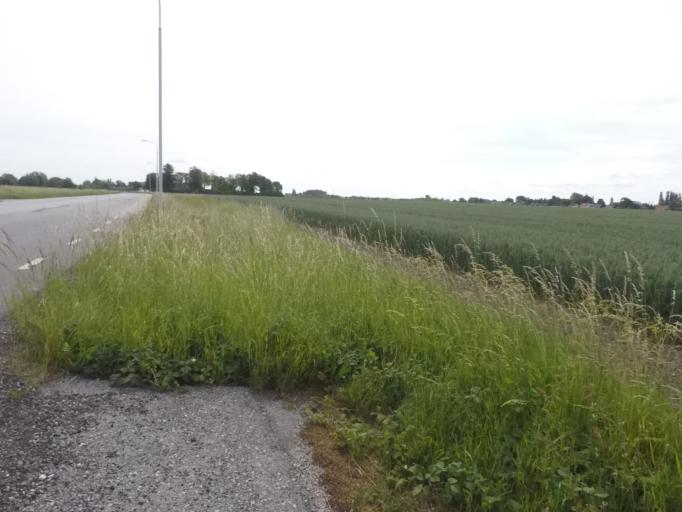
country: SE
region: Skane
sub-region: Malmo
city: Bunkeflostrand
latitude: 55.5441
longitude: 12.9581
